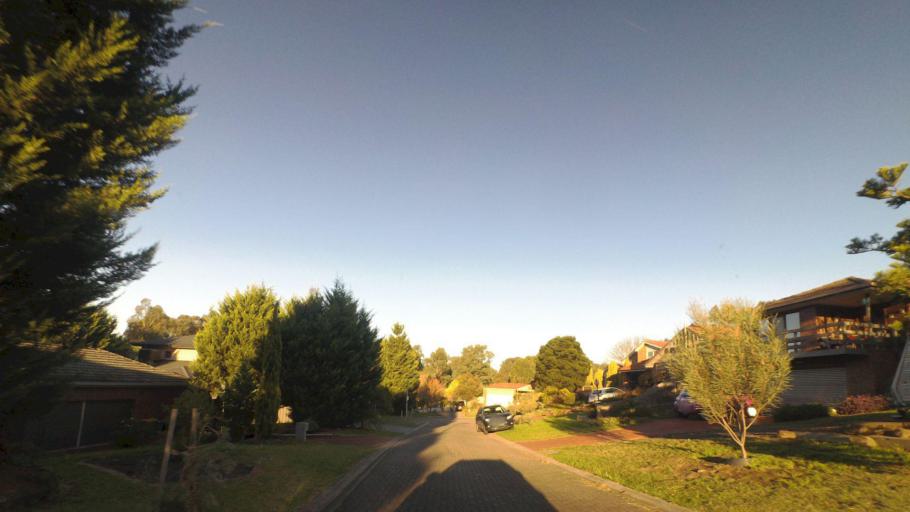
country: AU
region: Victoria
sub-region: Banyule
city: Viewbank
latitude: -37.7330
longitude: 145.1010
